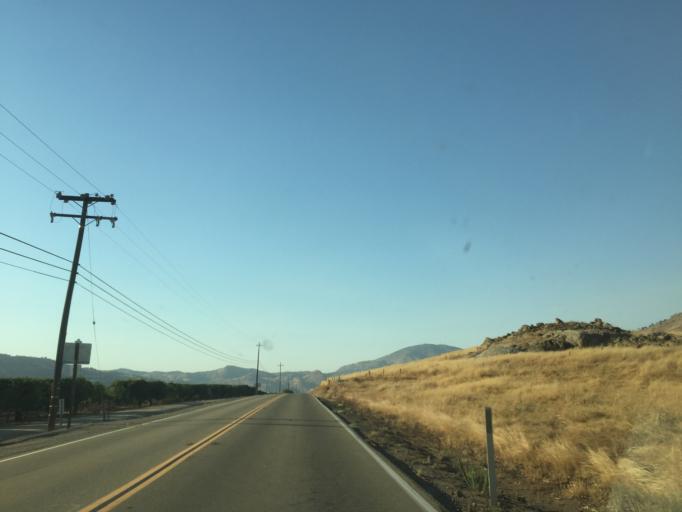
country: US
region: California
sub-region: Fresno County
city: Orange Cove
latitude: 36.6609
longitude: -119.3046
